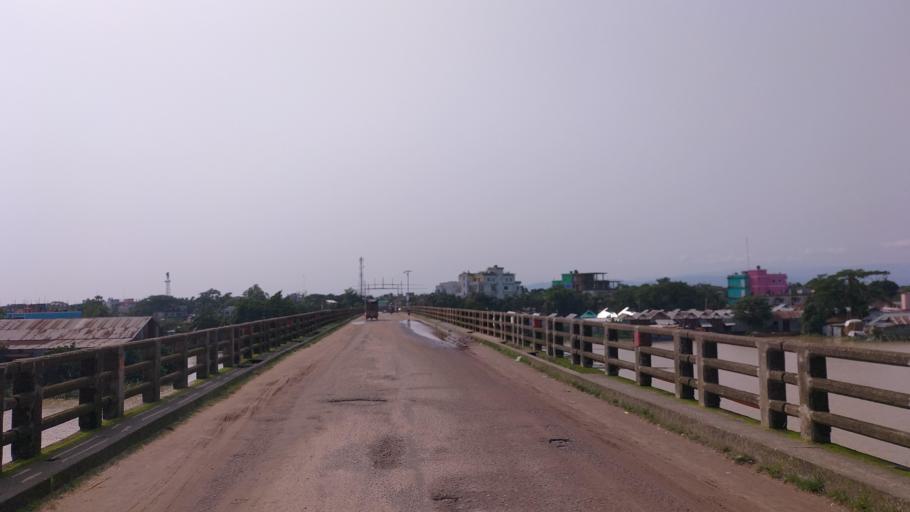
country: BD
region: Dhaka
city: Netrakona
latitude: 25.0747
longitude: 90.8908
